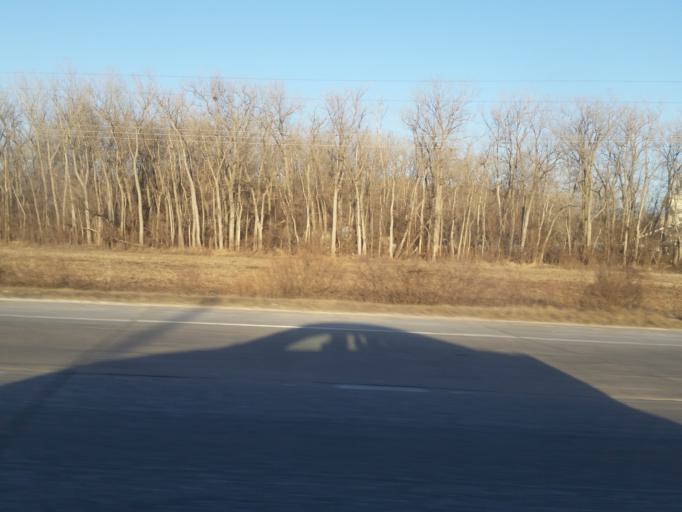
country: US
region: Nebraska
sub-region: Sarpy County
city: Offutt Air Force Base
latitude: 41.1442
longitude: -95.9384
